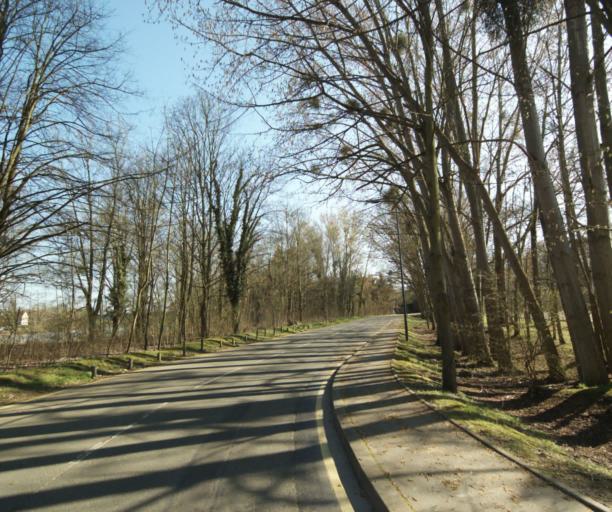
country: FR
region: Ile-de-France
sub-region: Departement du Val-d'Oise
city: Neuville-sur-Oise
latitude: 49.0295
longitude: 2.0588
